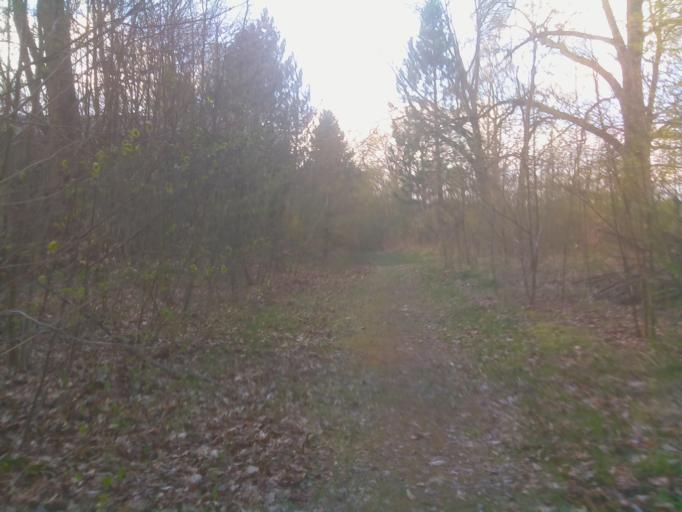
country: DE
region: Thuringia
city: Hummelshain
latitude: 50.7710
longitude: 11.6260
